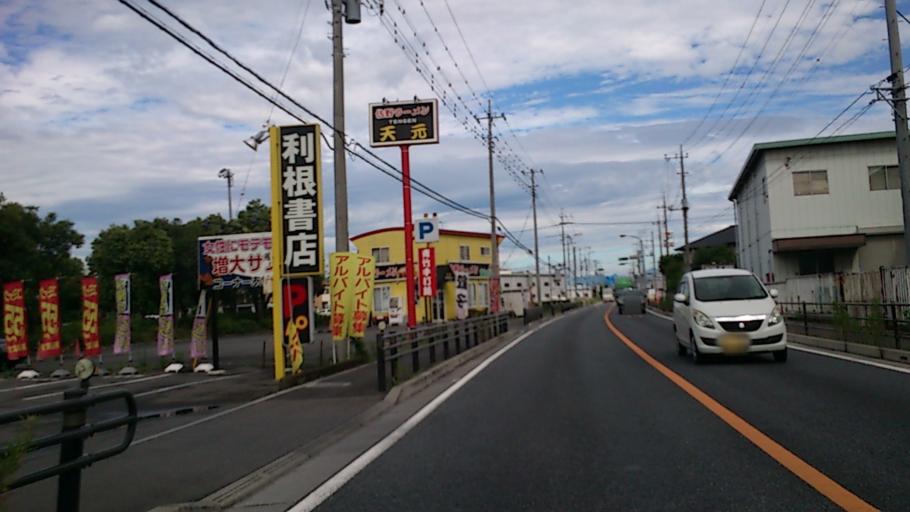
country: JP
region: Gunma
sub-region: Sawa-gun
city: Tamamura
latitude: 36.2623
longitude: 139.1365
